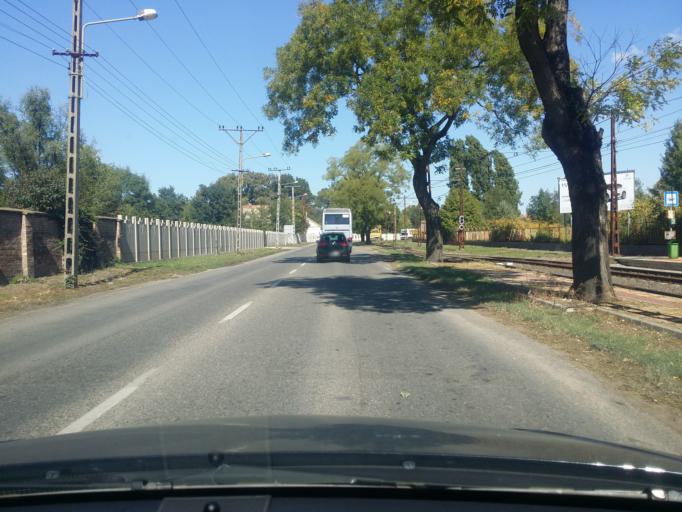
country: HU
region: Csongrad
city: Szeged
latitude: 46.2560
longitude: 20.1061
